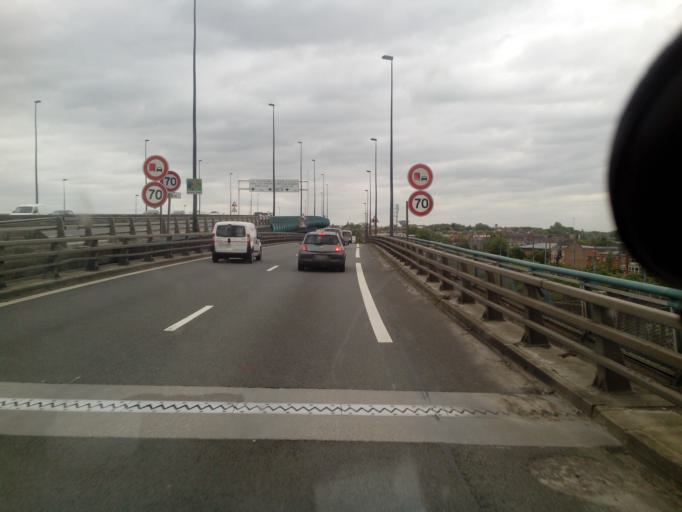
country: FR
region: Nord-Pas-de-Calais
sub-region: Departement du Nord
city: La Madeleine
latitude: 50.6302
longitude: 3.0824
